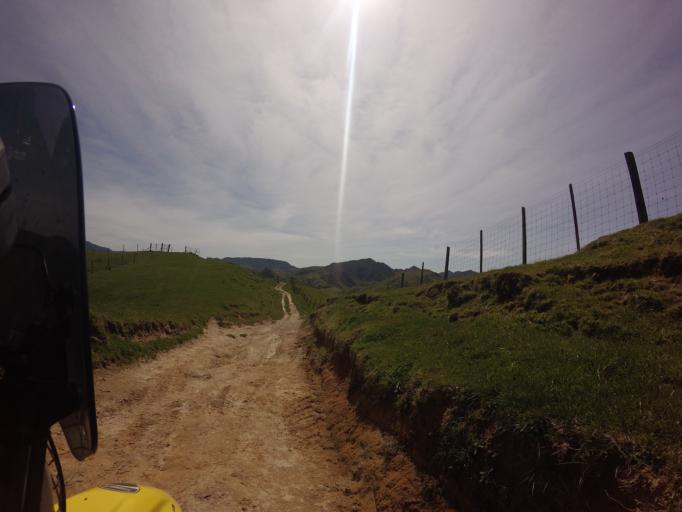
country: NZ
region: Bay of Plenty
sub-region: Opotiki District
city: Opotiki
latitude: -38.4692
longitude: 177.3788
